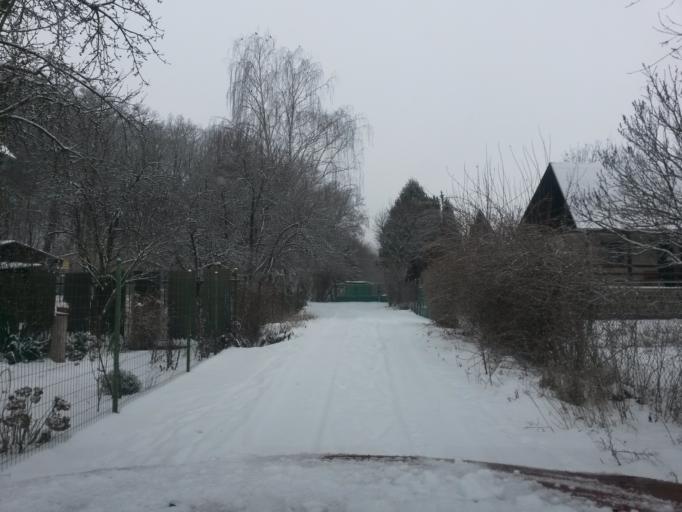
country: SK
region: Kosicky
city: Kosice
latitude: 48.7235
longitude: 21.3031
